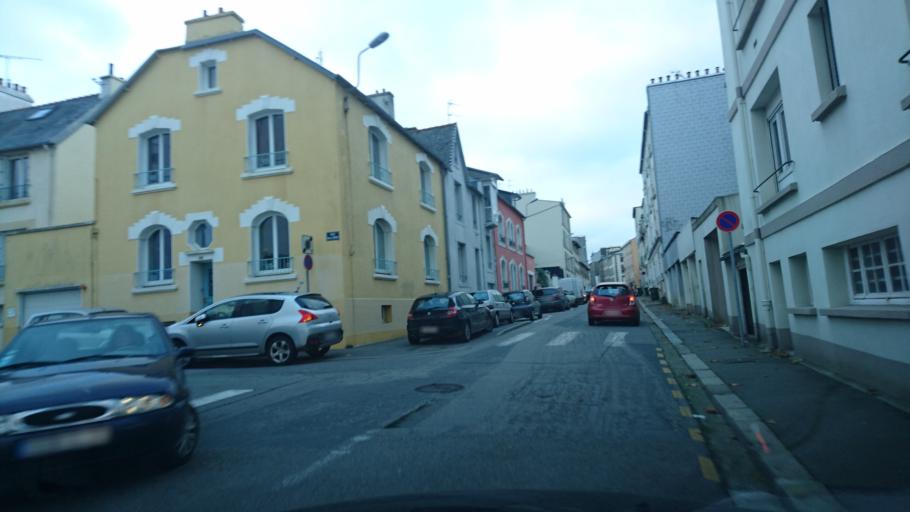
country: FR
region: Brittany
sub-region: Departement du Finistere
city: Brest
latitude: 48.3892
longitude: -4.4787
